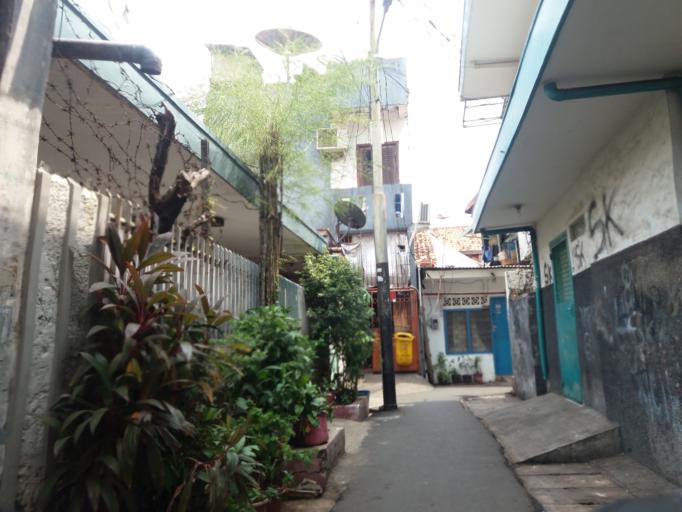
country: ID
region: Jakarta Raya
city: Jakarta
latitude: -6.1405
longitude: 106.8183
